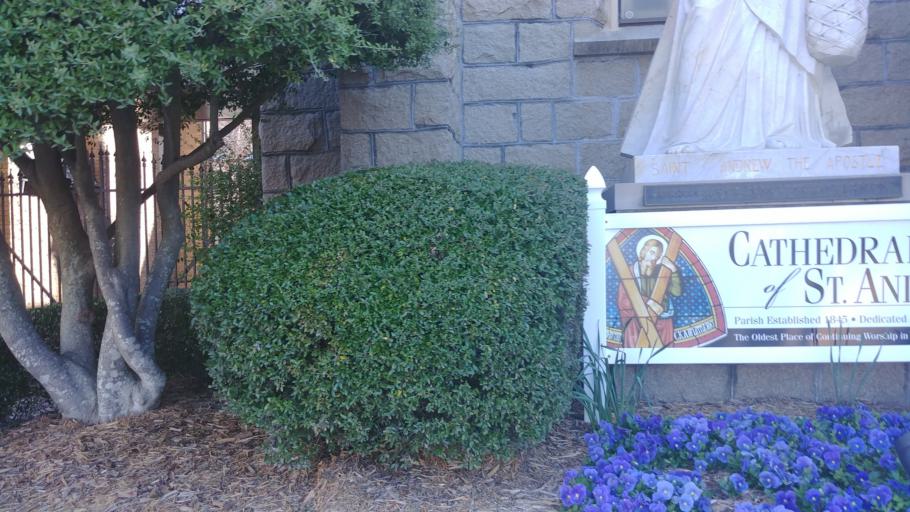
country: US
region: Arkansas
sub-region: Pulaski County
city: Little Rock
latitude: 34.7427
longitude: -92.2726
